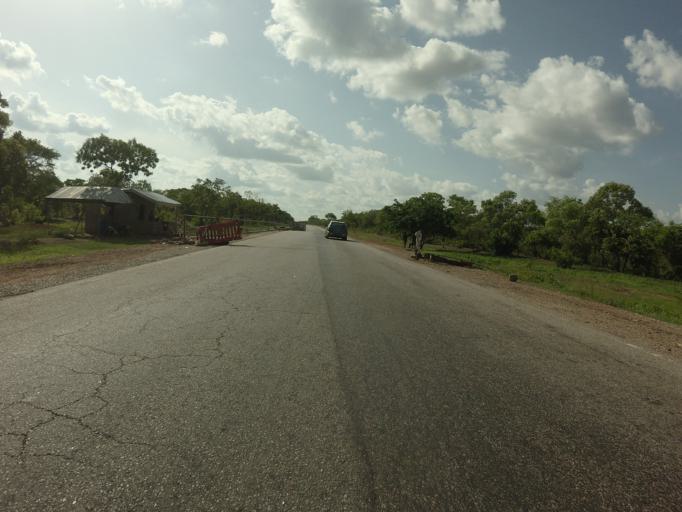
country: GH
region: Upper East
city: Bolgatanga
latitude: 10.5241
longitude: -0.8146
